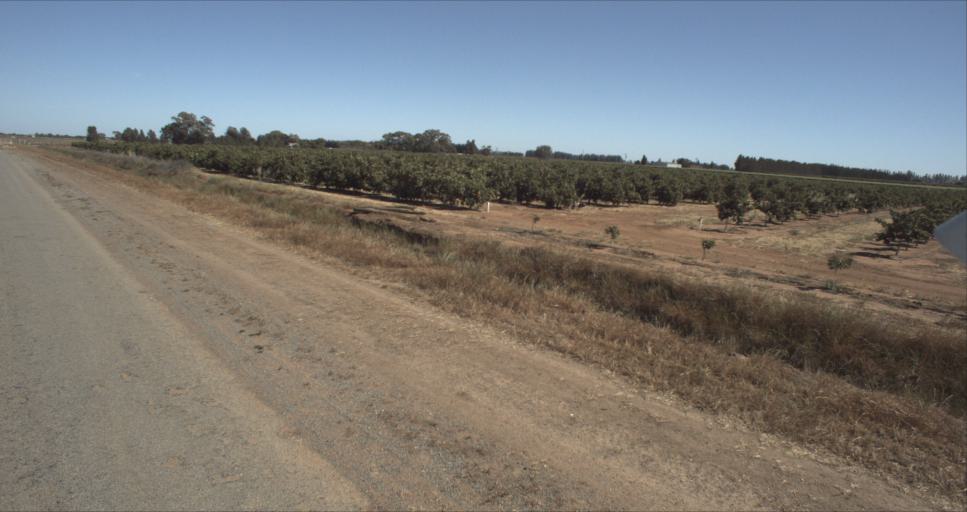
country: AU
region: New South Wales
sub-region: Leeton
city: Leeton
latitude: -34.5332
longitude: 146.3200
